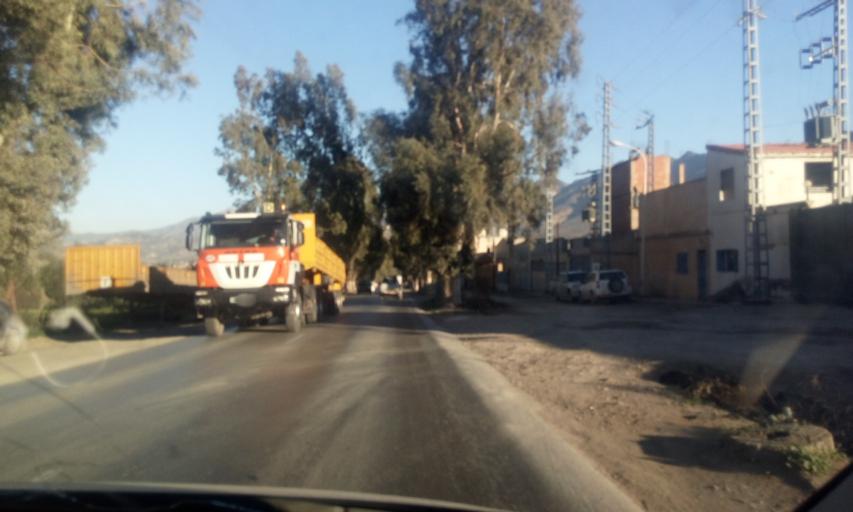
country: DZ
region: Bejaia
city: Akbou
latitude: 36.4830
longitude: 4.5640
